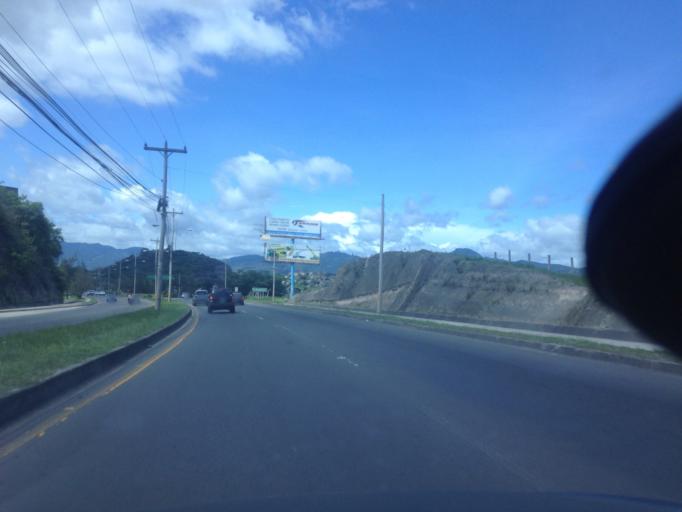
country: HN
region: Francisco Morazan
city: Yaguacire
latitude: 14.0464
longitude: -87.2154
